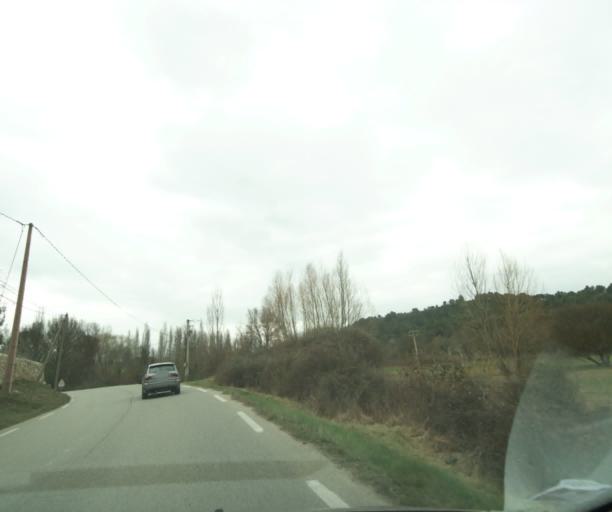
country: FR
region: Provence-Alpes-Cote d'Azur
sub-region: Departement des Bouches-du-Rhone
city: Jouques
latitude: 43.6320
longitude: 5.6529
